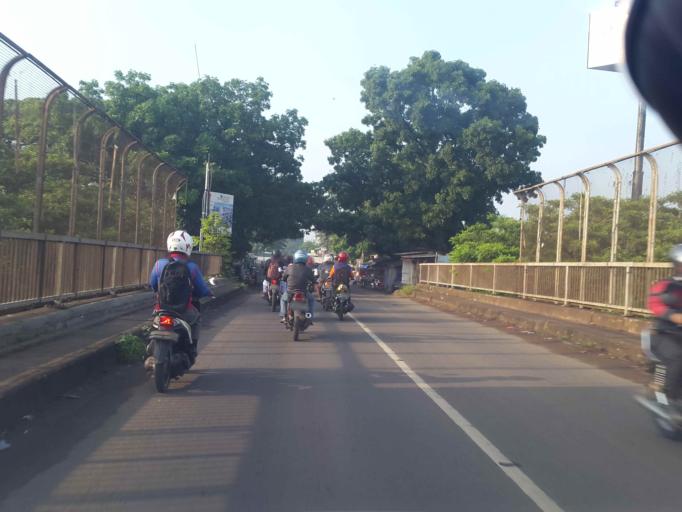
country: ID
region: West Java
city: Cikarang
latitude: -6.2824
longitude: 107.0729
